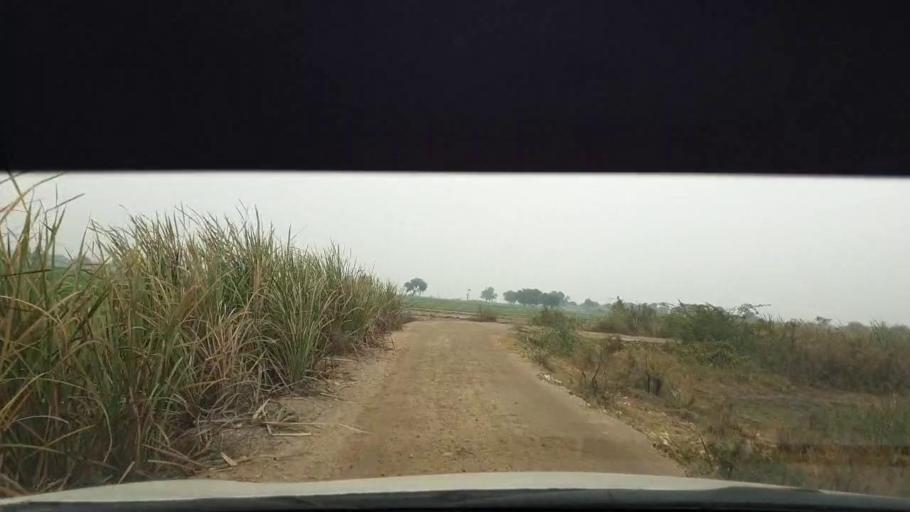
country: PK
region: Sindh
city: Berani
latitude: 25.7695
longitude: 68.7666
